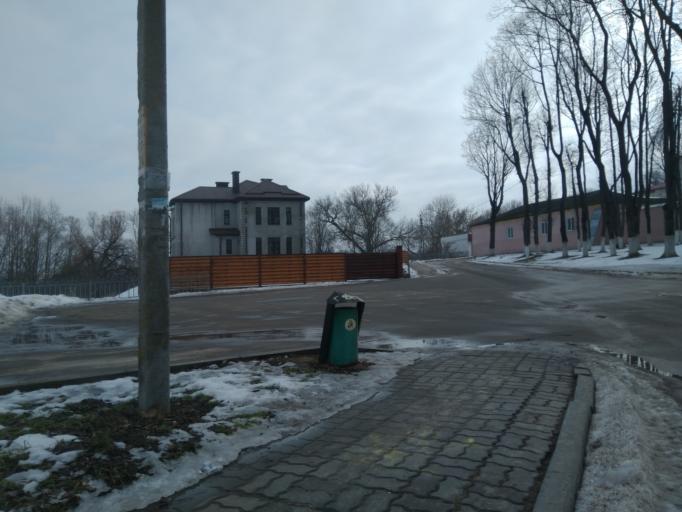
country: BY
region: Minsk
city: Nyasvizh
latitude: 53.2167
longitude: 26.6820
